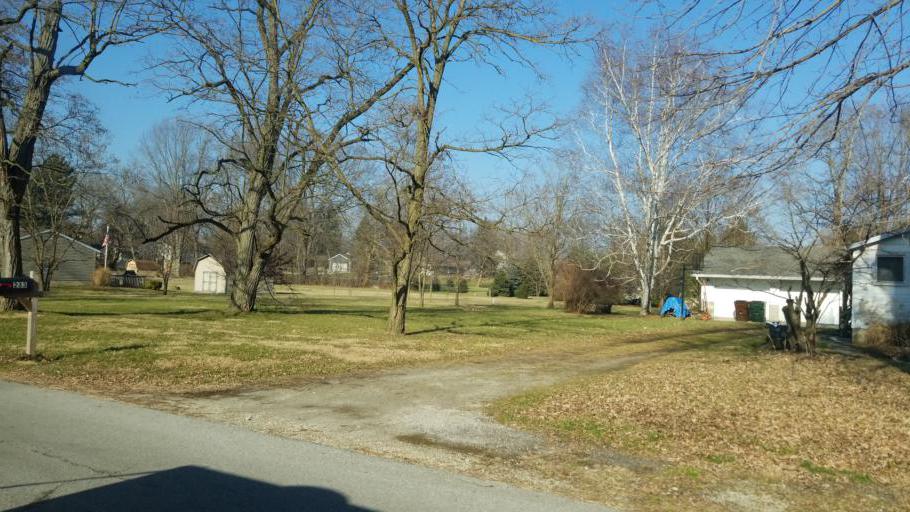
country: US
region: Ohio
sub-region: Seneca County
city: Tiffin
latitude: 41.1289
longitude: -83.1675
